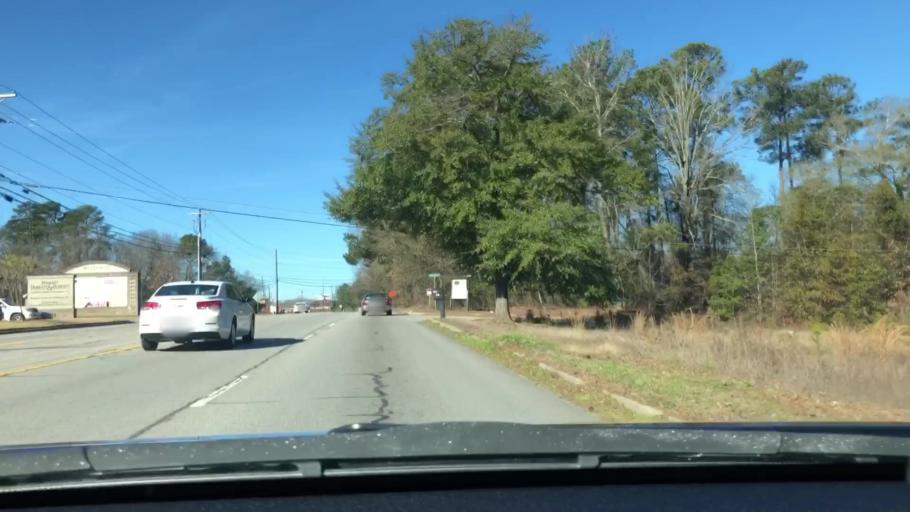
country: US
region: South Carolina
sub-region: Lexington County
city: Oak Grove
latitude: 34.0071
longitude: -81.1237
